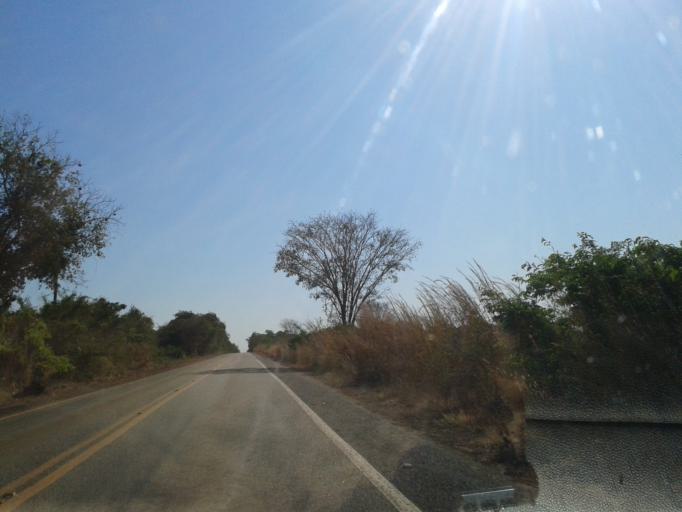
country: BR
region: Goias
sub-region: Mozarlandia
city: Mozarlandia
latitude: -14.6820
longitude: -50.5391
